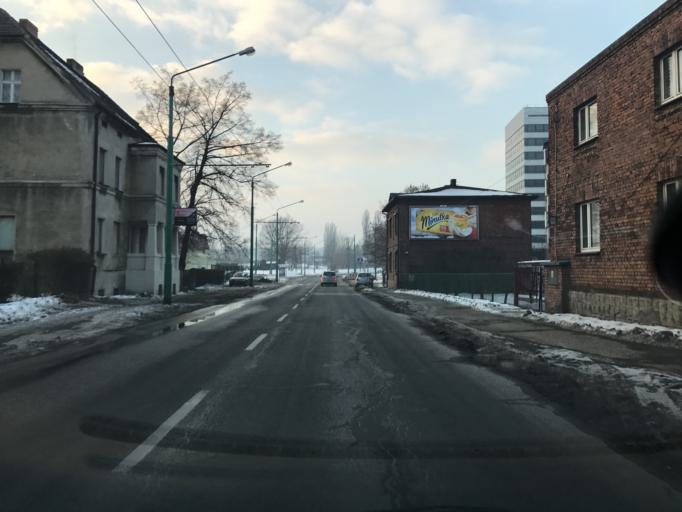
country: PL
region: Silesian Voivodeship
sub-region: Tychy
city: Tychy
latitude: 50.1291
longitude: 18.9681
